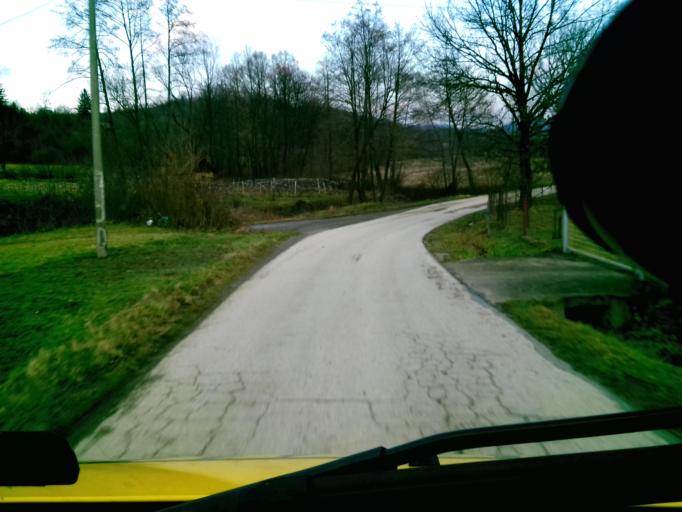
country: BA
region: Federation of Bosnia and Herzegovina
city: Novi Seher
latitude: 44.4730
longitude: 18.0418
